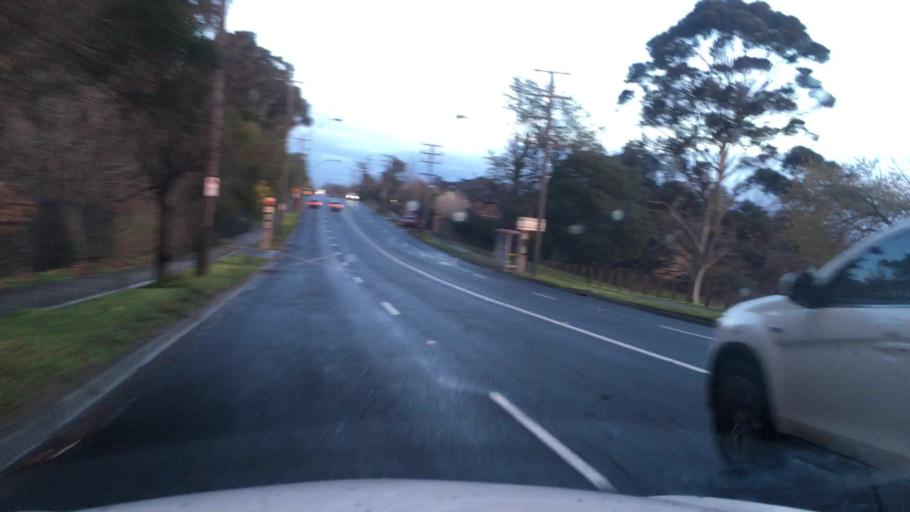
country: AU
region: Victoria
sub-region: Whitehorse
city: Surrey Hills
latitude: -37.8389
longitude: 145.0977
